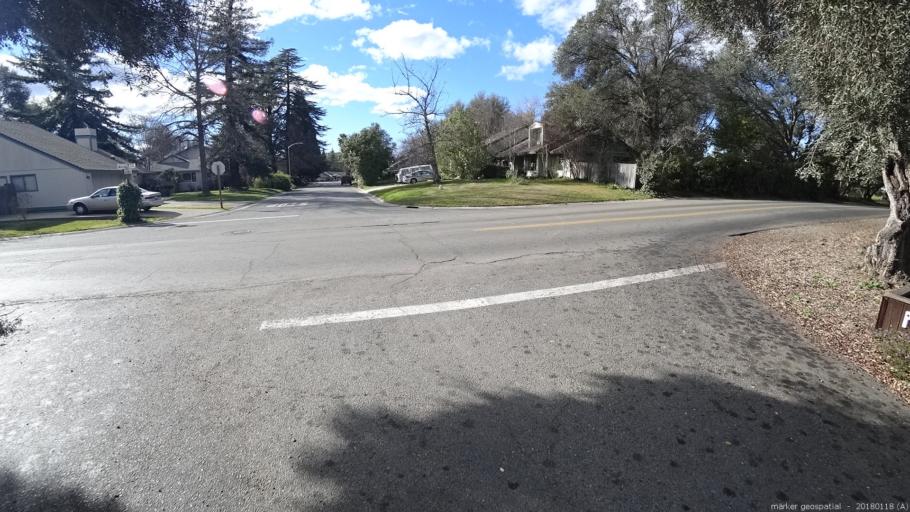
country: US
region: California
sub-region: Sacramento County
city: Orangevale
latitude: 38.6841
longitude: -121.2066
